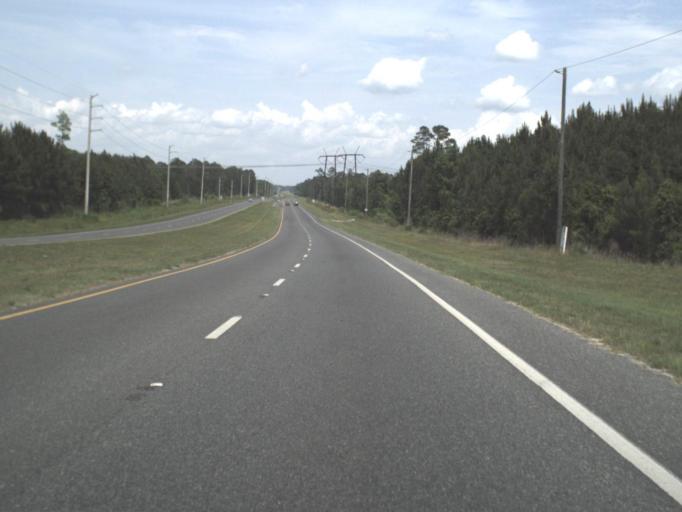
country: US
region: Florida
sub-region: Putnam County
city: Interlachen
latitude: 29.6261
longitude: -81.7912
